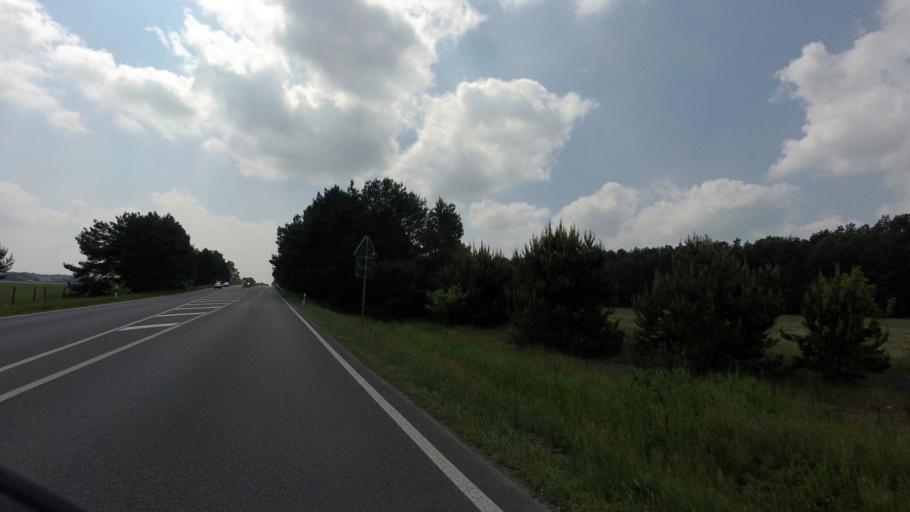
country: DE
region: Brandenburg
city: Cottbus
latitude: 51.6921
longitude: 14.3602
